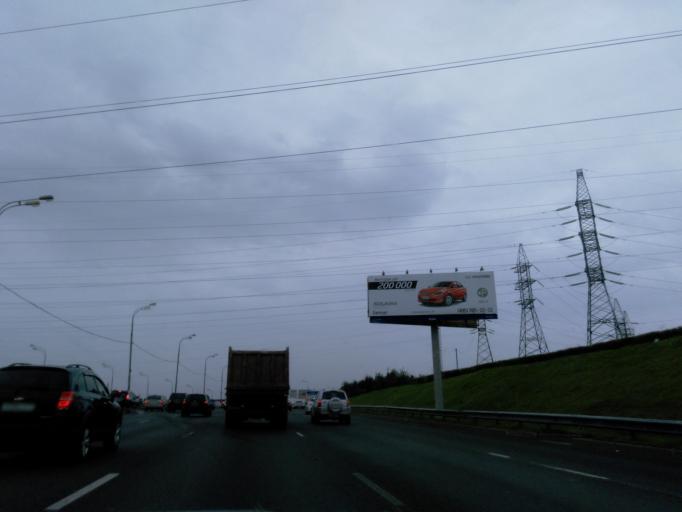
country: RU
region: Moscow
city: Strogino
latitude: 55.8379
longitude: 37.3955
